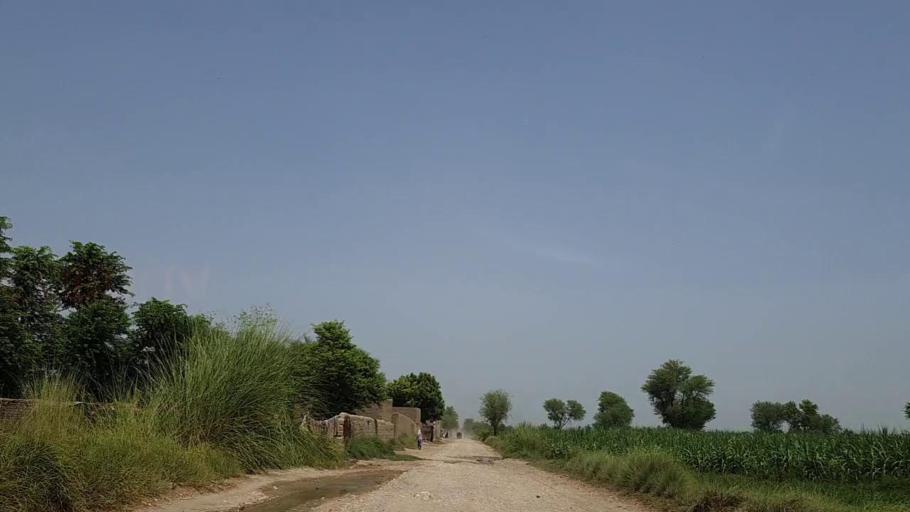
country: PK
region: Sindh
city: Tharu Shah
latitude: 26.9009
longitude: 68.0075
